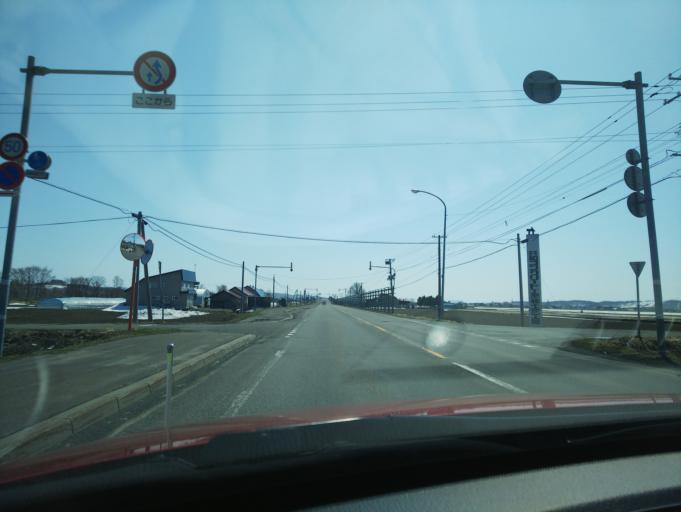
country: JP
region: Hokkaido
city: Nayoro
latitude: 44.2010
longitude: 142.3949
